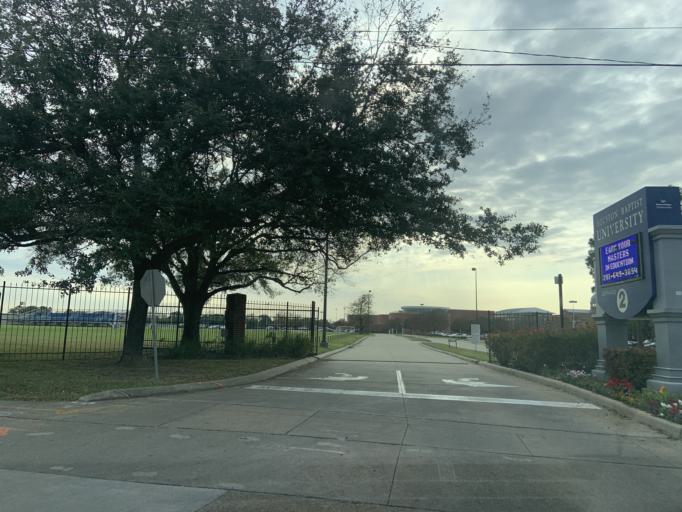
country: US
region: Texas
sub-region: Harris County
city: Bellaire
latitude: 29.6952
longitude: -95.5121
